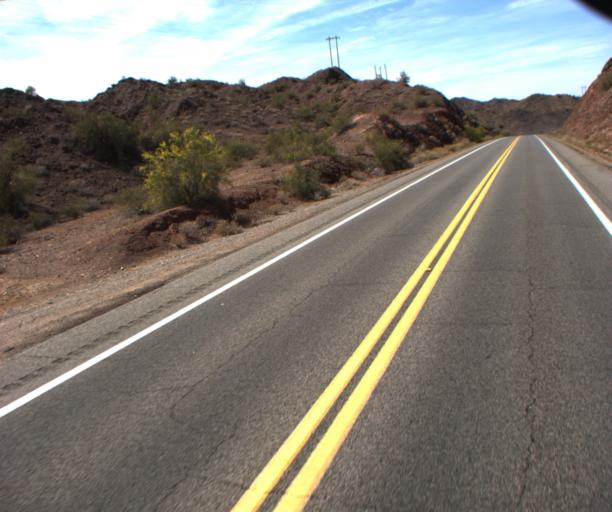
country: US
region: Arizona
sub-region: La Paz County
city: Cienega Springs
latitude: 34.3490
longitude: -114.1522
